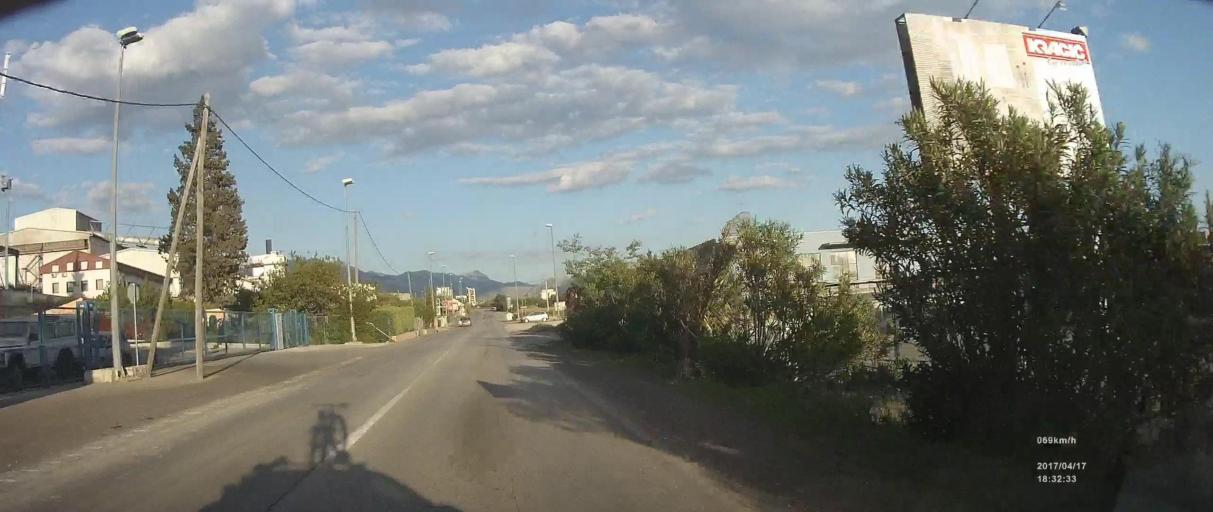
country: HR
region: Splitsko-Dalmatinska
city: Vranjic
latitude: 43.5421
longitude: 16.4475
